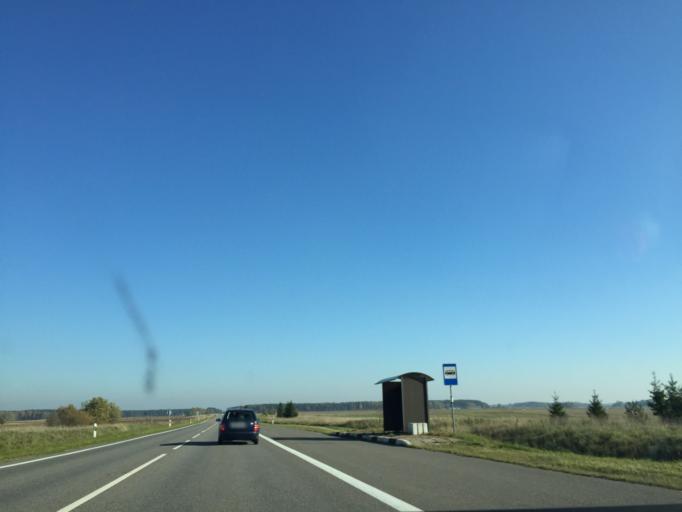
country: LT
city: Salantai
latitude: 55.9243
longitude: 21.5454
